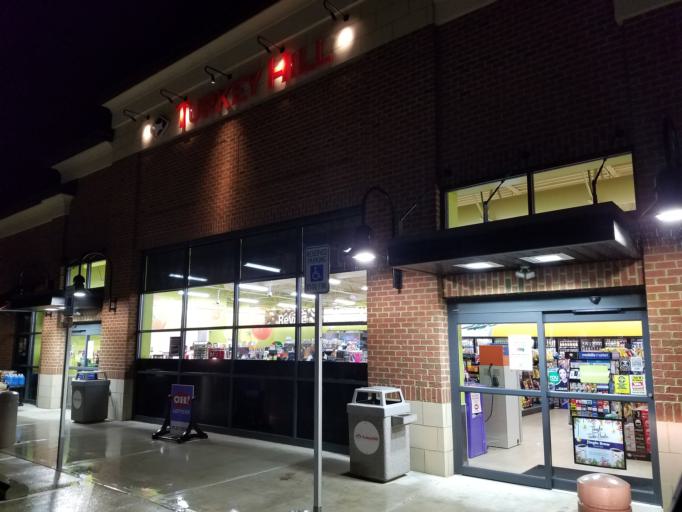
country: US
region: Ohio
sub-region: Franklin County
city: New Albany
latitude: 40.0908
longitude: -82.7912
